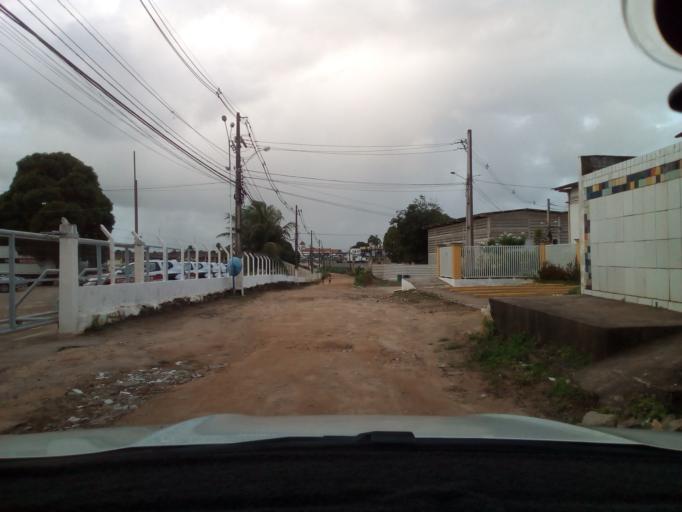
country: BR
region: Paraiba
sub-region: Bayeux
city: Bayeux
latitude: -7.1594
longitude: -34.9094
